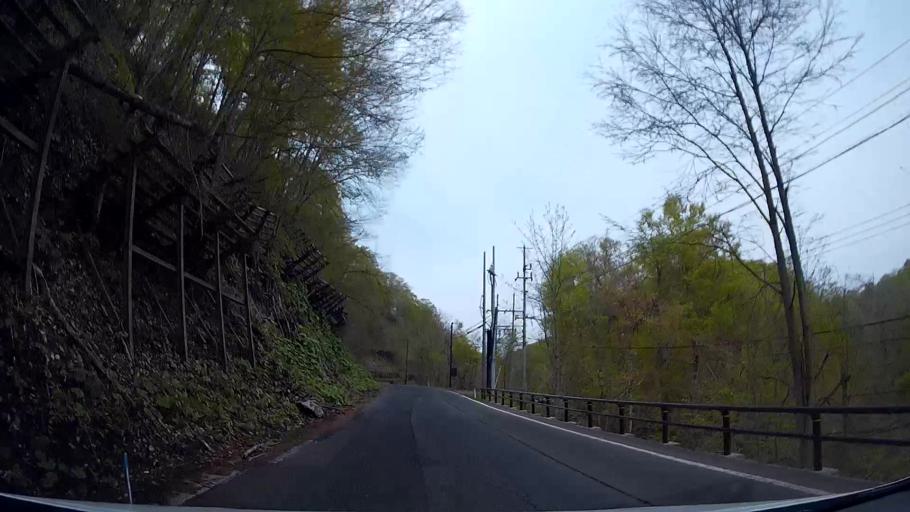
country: JP
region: Akita
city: Hanawa
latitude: 40.3908
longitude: 140.8798
